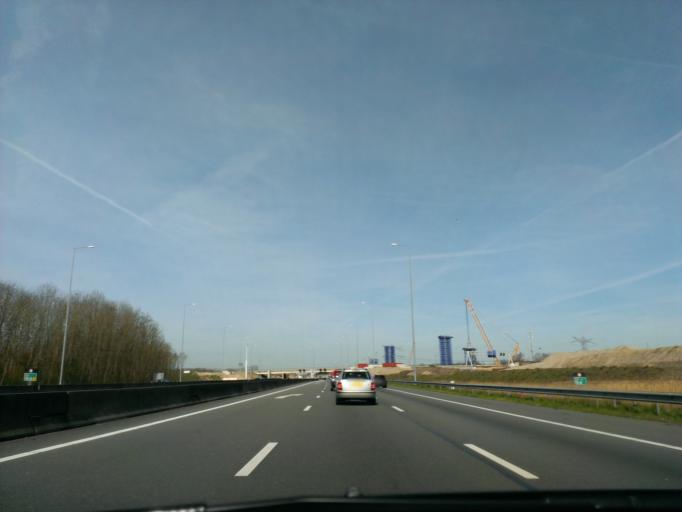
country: NL
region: North Holland
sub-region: Gemeente Naarden
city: Naarden
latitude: 52.3132
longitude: 5.1118
